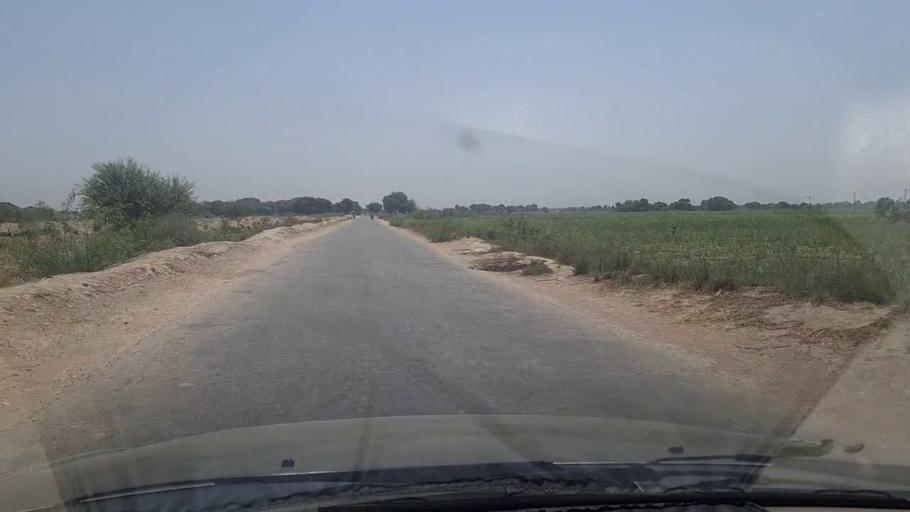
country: PK
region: Sindh
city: Chambar
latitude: 25.2692
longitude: 68.6374
